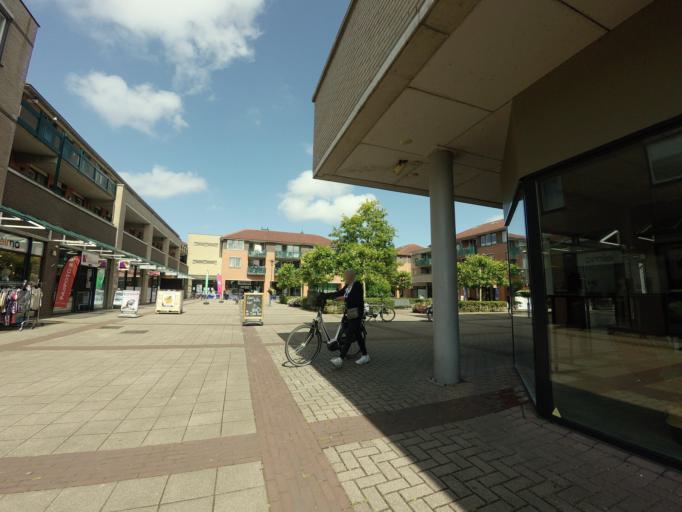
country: NL
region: North Holland
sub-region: Gemeente Schagen
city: Schagen
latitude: 52.8614
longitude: 4.8318
